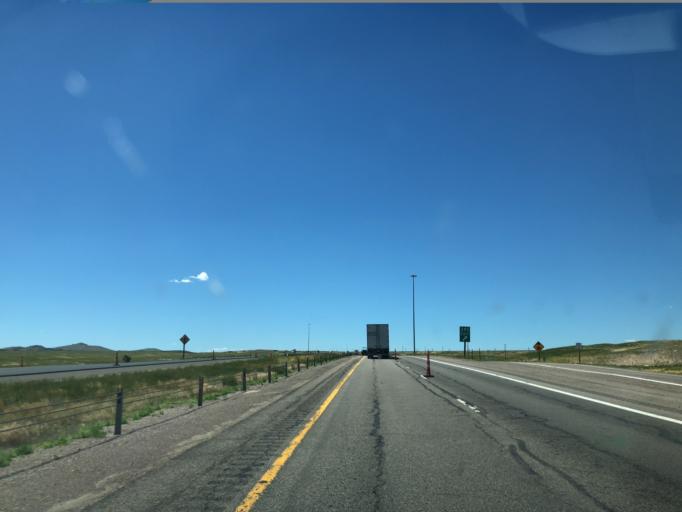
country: US
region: Wyoming
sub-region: Laramie County
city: Cheyenne
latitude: 41.0980
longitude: -105.1129
